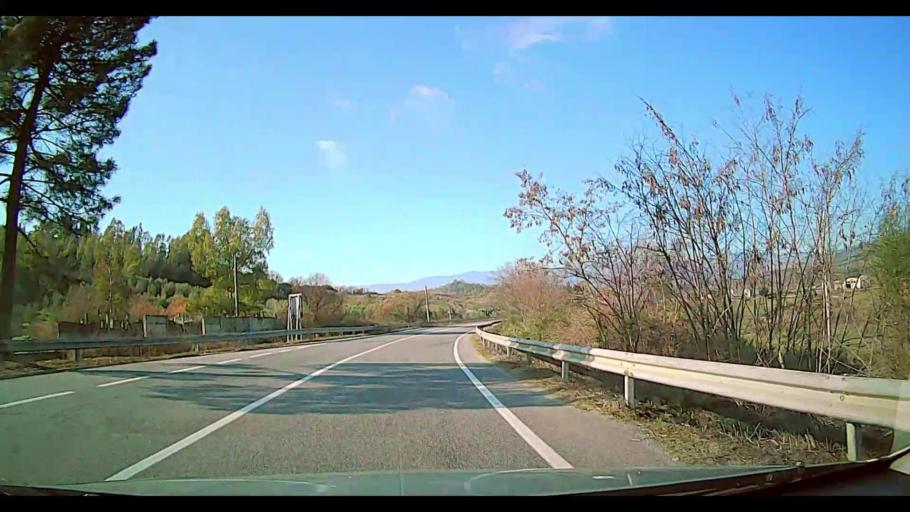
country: IT
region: Calabria
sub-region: Provincia di Crotone
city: Belvedere Spinello
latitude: 39.1892
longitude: 16.8769
